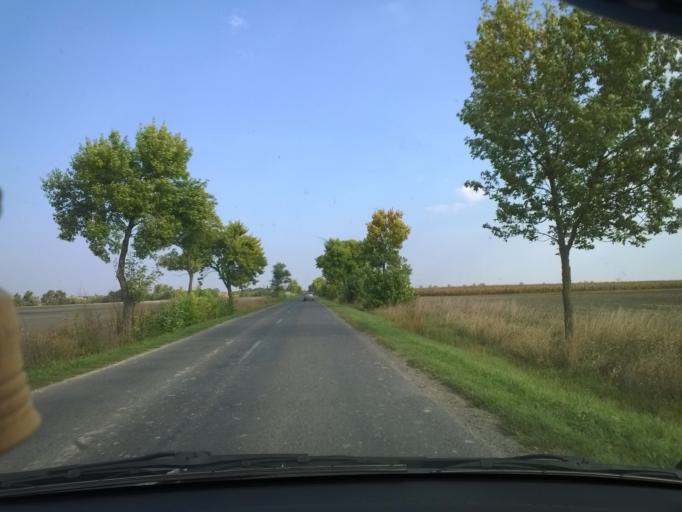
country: HU
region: Bacs-Kiskun
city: Kalocsa
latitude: 46.4946
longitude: 19.0522
